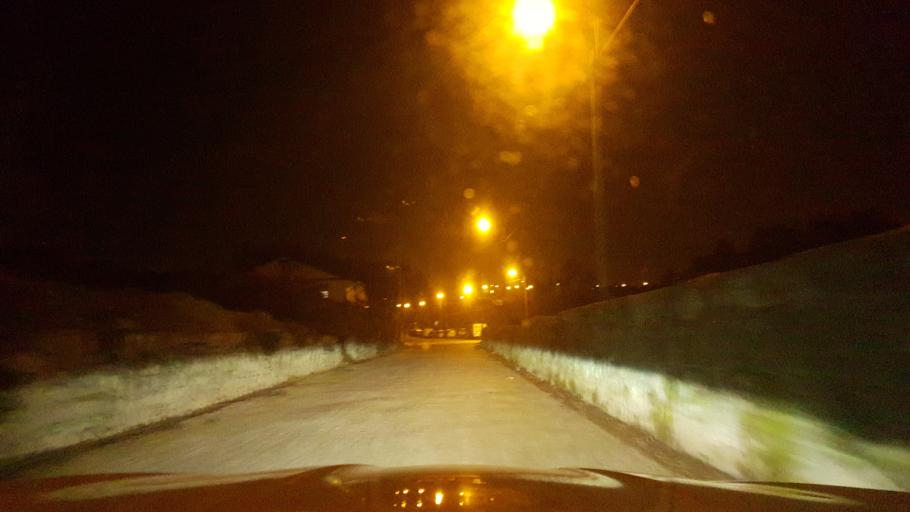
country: PT
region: Porto
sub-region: Matosinhos
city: Guifoes
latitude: 41.2180
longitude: -8.6603
